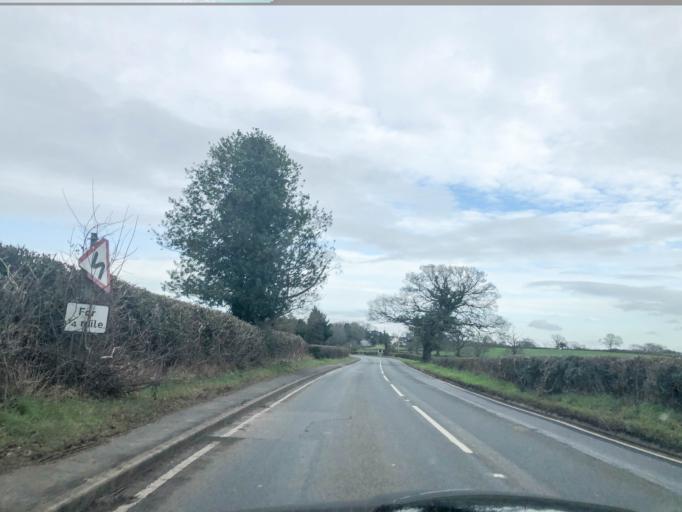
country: GB
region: England
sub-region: Warwickshire
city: Wroxall
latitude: 52.3022
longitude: -1.6721
